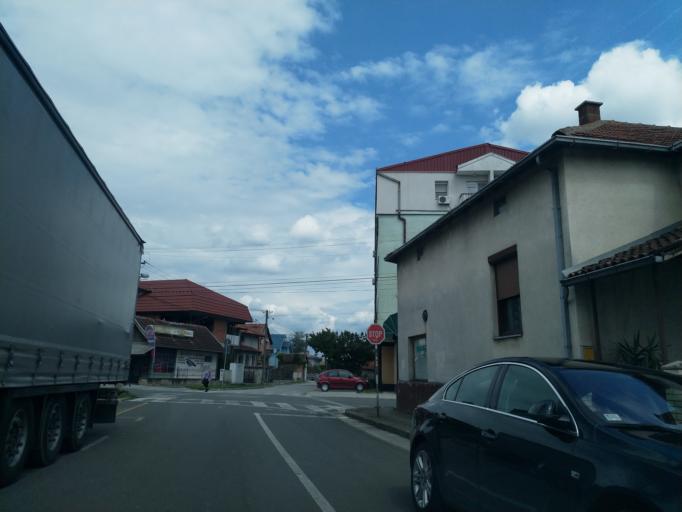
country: RS
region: Central Serbia
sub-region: Pomoravski Okrug
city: Cuprija
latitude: 43.9358
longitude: 21.3724
